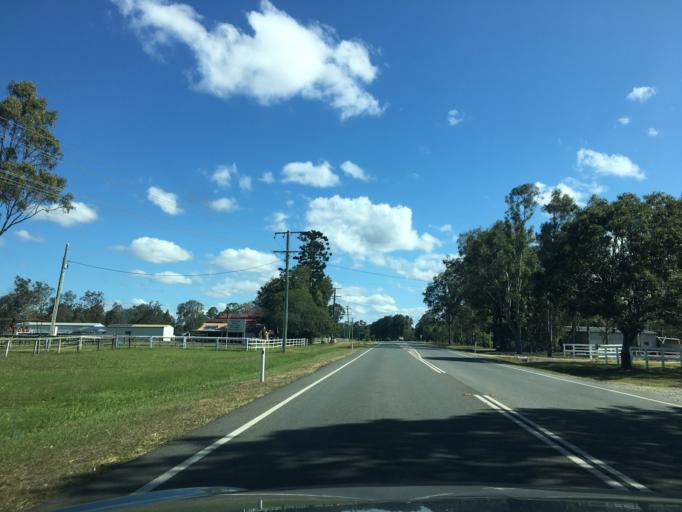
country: AU
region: Queensland
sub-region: Logan
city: Waterford West
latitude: -27.7125
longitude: 153.1304
